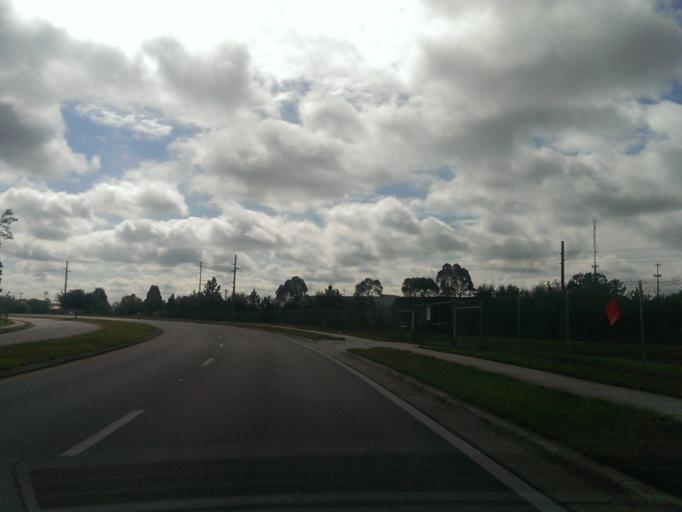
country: US
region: Florida
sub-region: Orange County
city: Doctor Phillips
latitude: 28.3996
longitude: -81.5322
